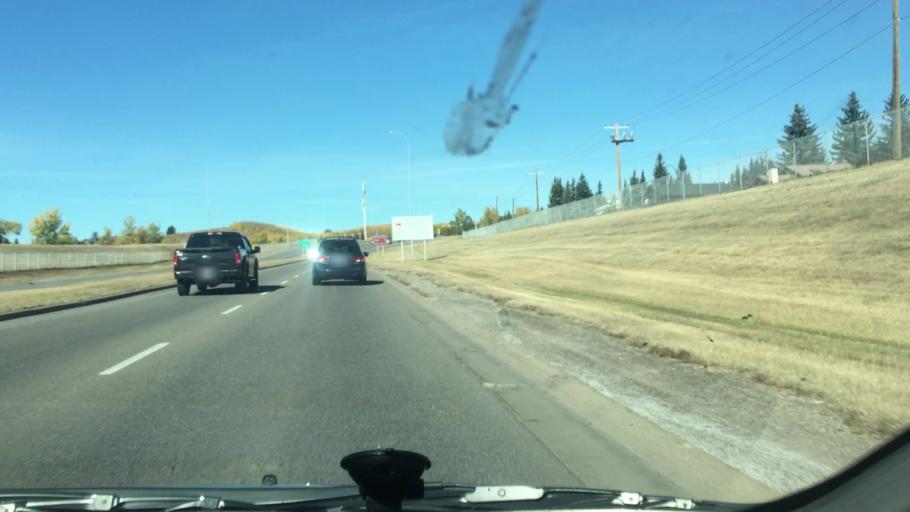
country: CA
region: Alberta
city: Calgary
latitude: 51.1182
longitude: -114.1616
